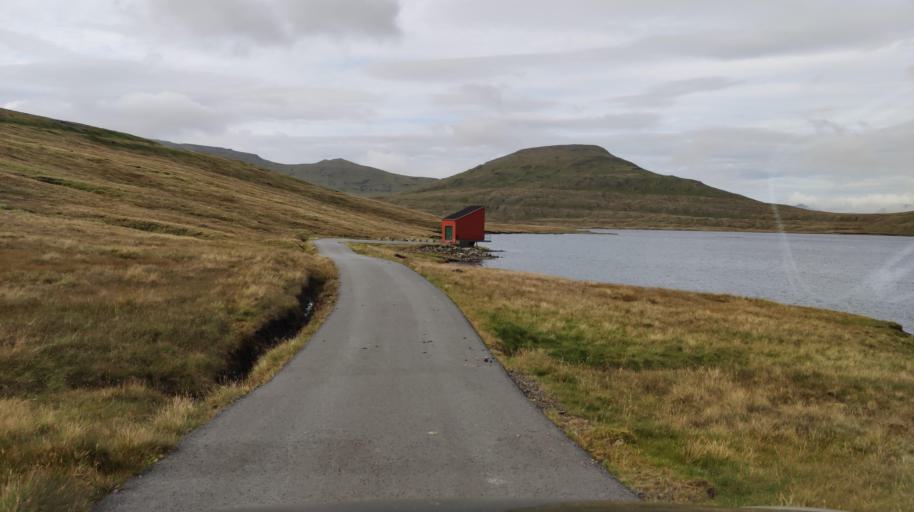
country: FO
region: Streymoy
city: Vestmanna
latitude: 62.1637
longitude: -7.0906
